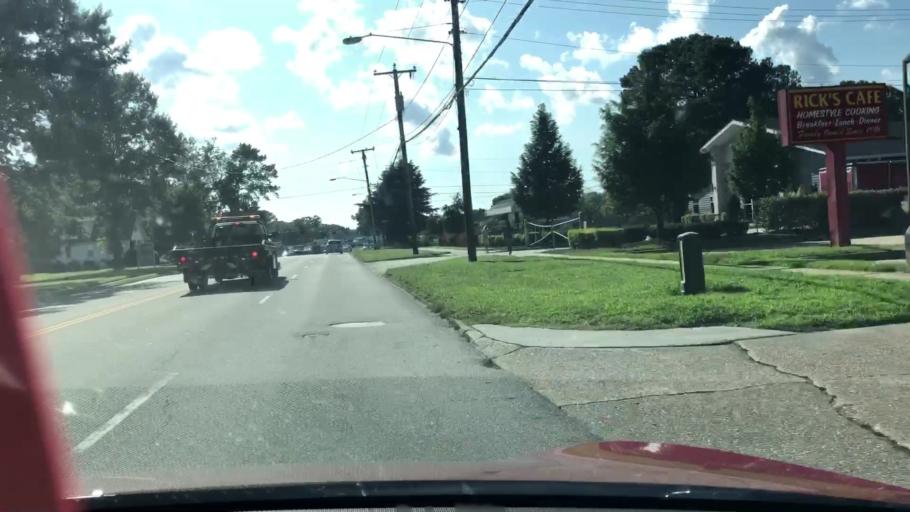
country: US
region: Virginia
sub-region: City of Virginia Beach
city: Virginia Beach
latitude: 36.8424
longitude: -76.0186
